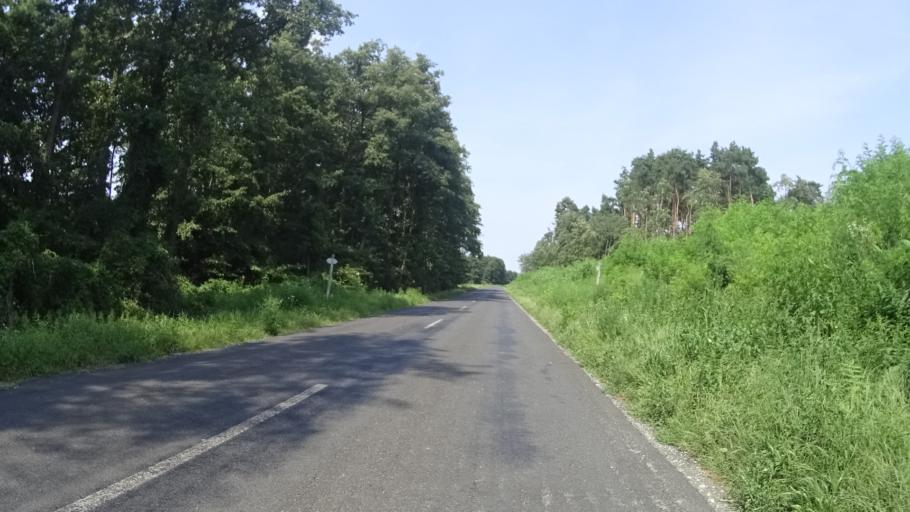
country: HU
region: Zala
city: Murakeresztur
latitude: 46.3835
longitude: 16.9239
